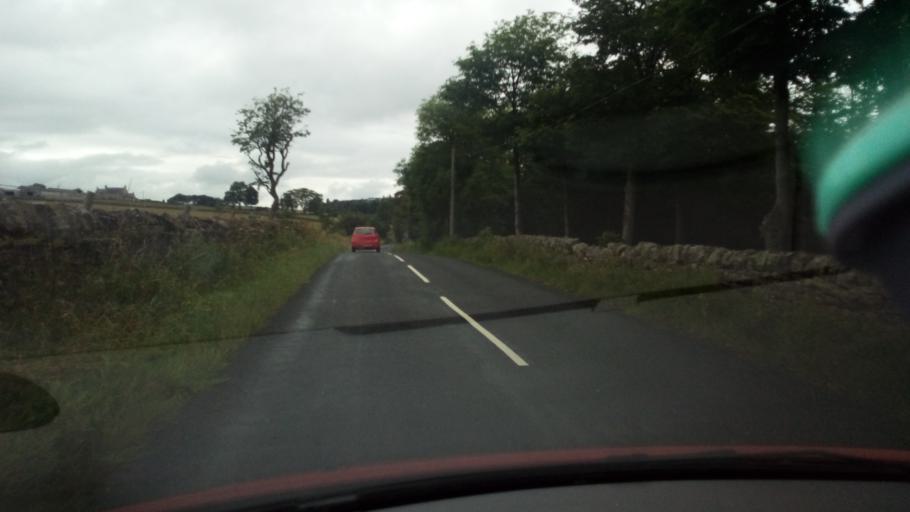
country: GB
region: England
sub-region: Northumberland
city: Slaley
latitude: 54.8466
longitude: -2.0459
